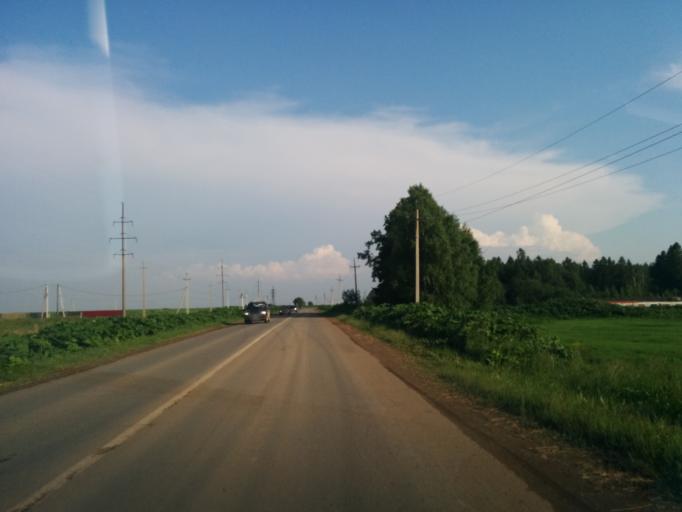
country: RU
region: Perm
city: Polazna
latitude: 58.2254
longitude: 56.2943
